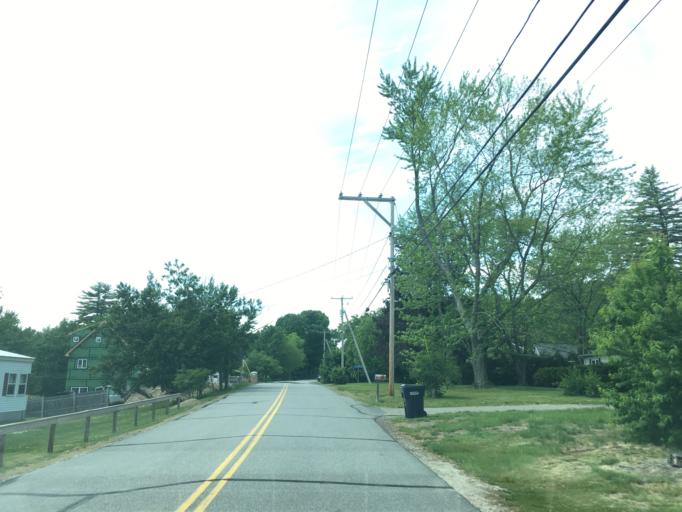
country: US
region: New Hampshire
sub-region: Rockingham County
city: Stratham Station
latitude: 43.0330
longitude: -70.8754
